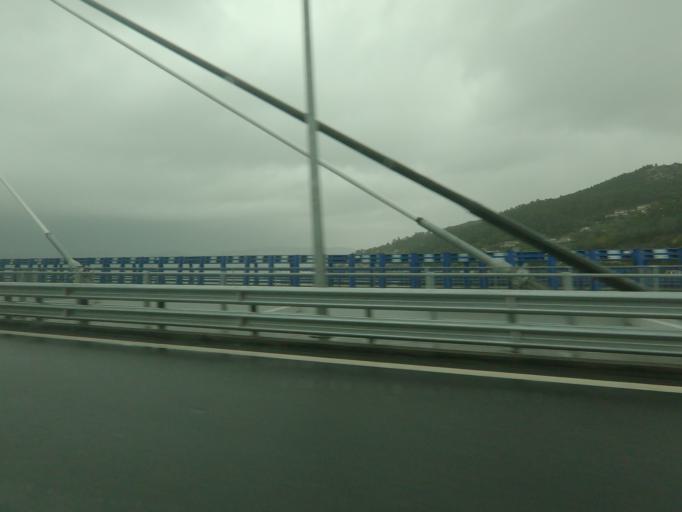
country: ES
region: Galicia
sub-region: Provincia de Pontevedra
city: Redondela
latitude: 42.2859
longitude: -8.6606
